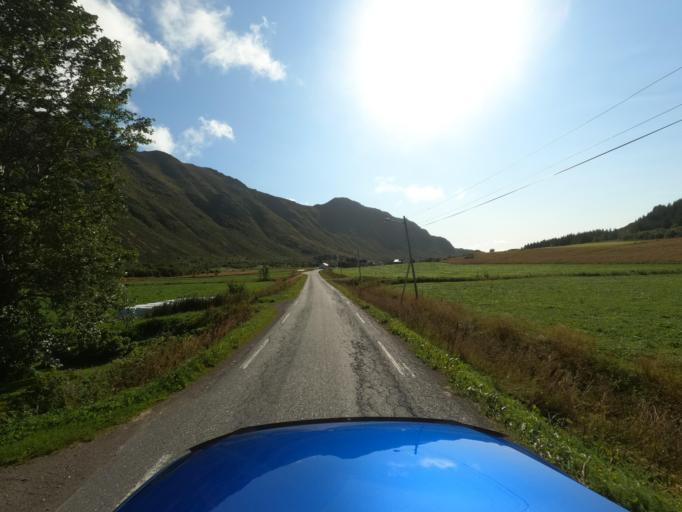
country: NO
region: Nordland
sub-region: Vestvagoy
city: Leknes
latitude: 68.1057
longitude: 13.6539
